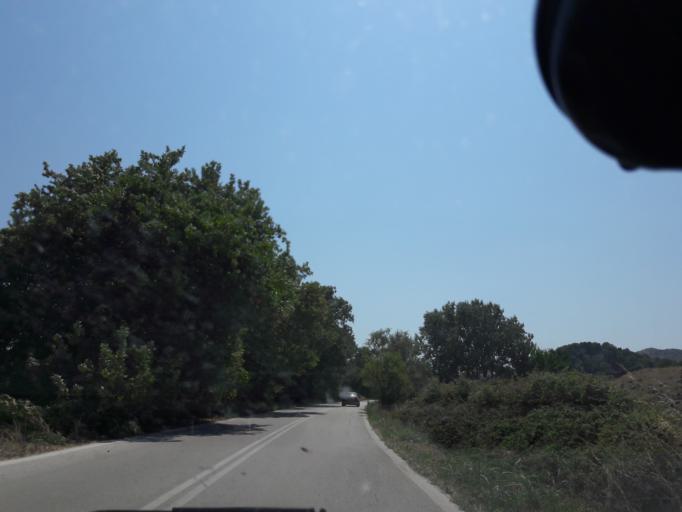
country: GR
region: North Aegean
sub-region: Nomos Lesvou
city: Myrina
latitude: 39.8706
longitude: 25.1575
